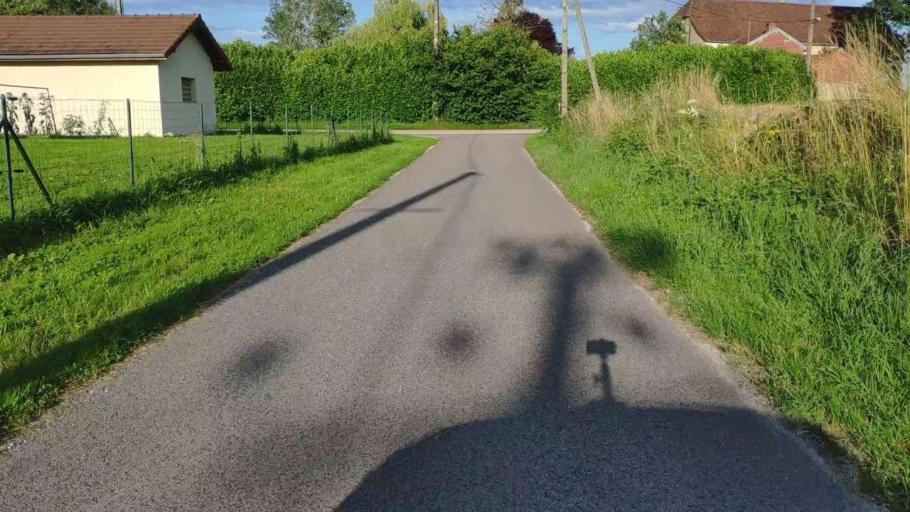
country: FR
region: Franche-Comte
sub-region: Departement du Jura
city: Bletterans
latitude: 46.7822
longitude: 5.4922
